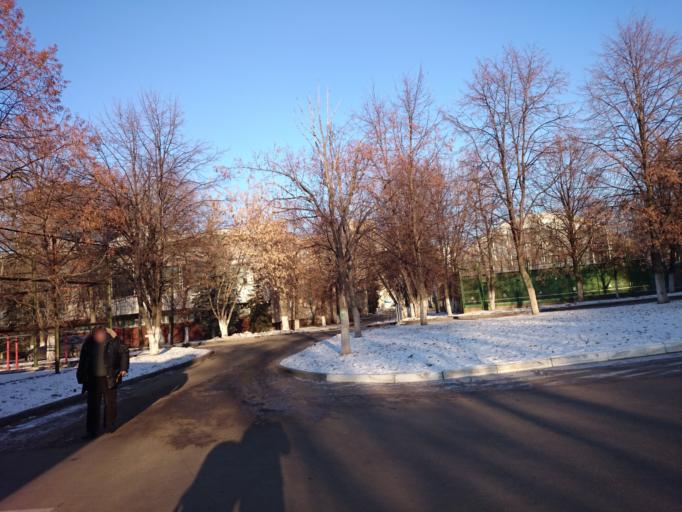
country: RU
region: Moscow
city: Sokol
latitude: 55.7927
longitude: 37.5365
